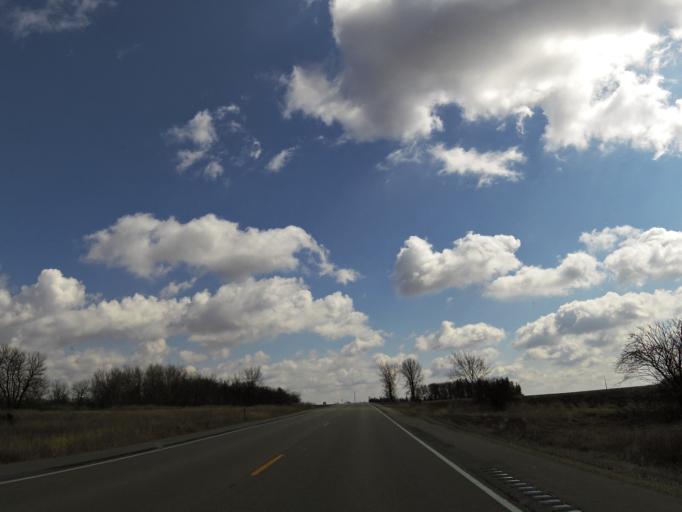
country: US
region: Minnesota
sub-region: Goodhue County
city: Kenyon
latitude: 44.2436
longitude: -92.9614
